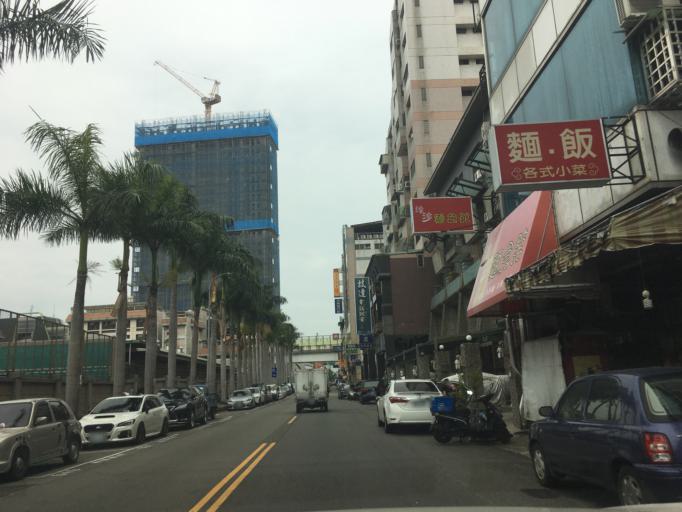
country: TW
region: Taiwan
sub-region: Taichung City
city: Taichung
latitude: 24.1702
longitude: 120.6621
